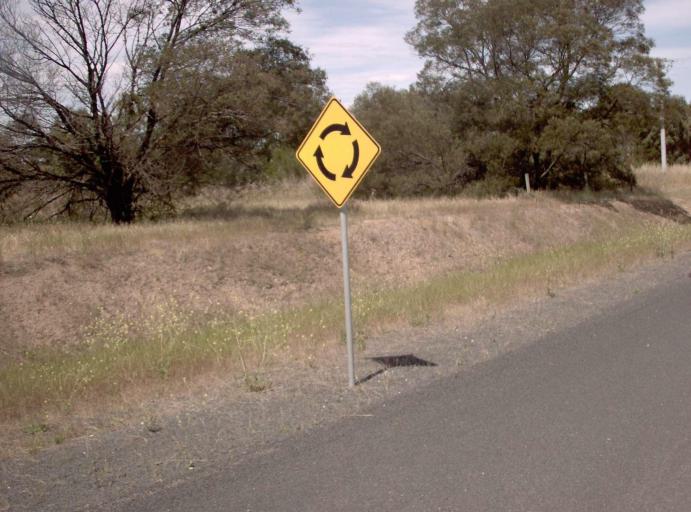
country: AU
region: Victoria
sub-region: Wellington
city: Sale
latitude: -38.1069
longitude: 147.0363
